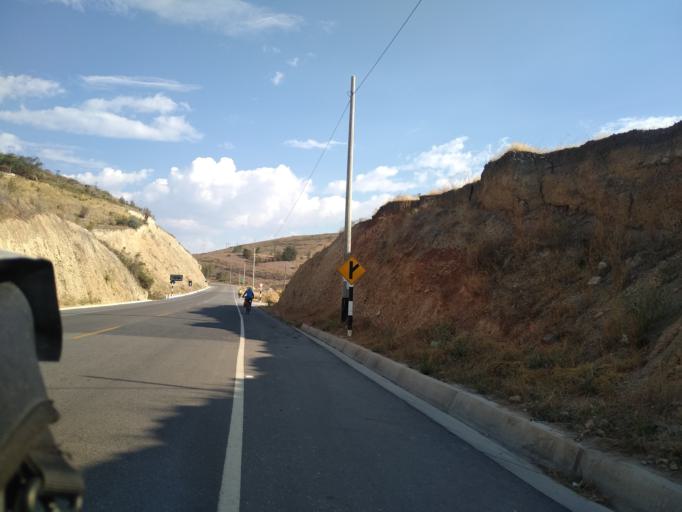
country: PE
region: Cajamarca
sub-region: San Marcos
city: San Marcos
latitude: -7.3741
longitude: -78.1287
